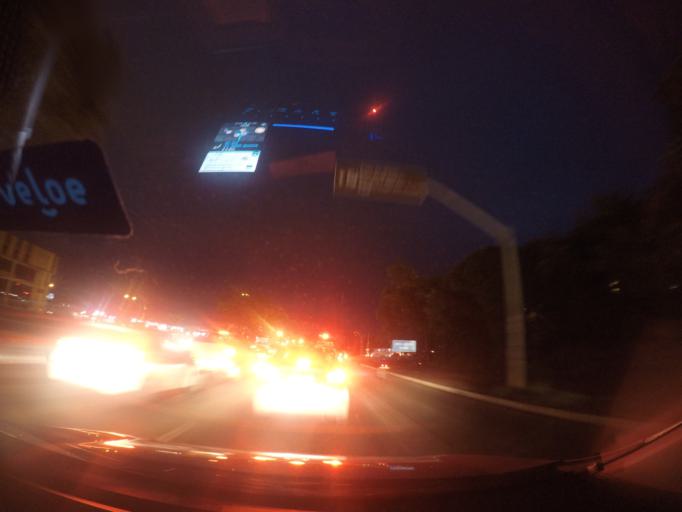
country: BR
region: Goias
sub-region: Goiania
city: Goiania
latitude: -16.6247
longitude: -49.2531
